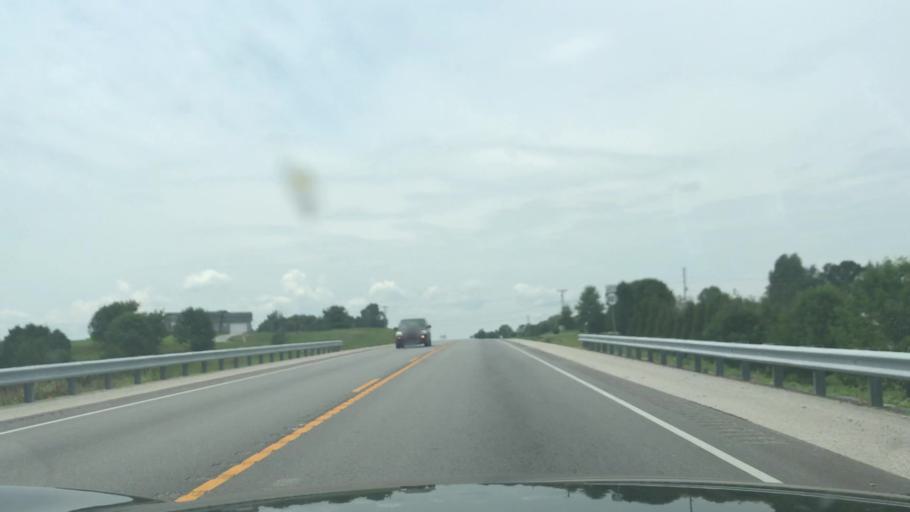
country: US
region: Kentucky
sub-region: Taylor County
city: Campbellsville
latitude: 37.3168
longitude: -85.4154
